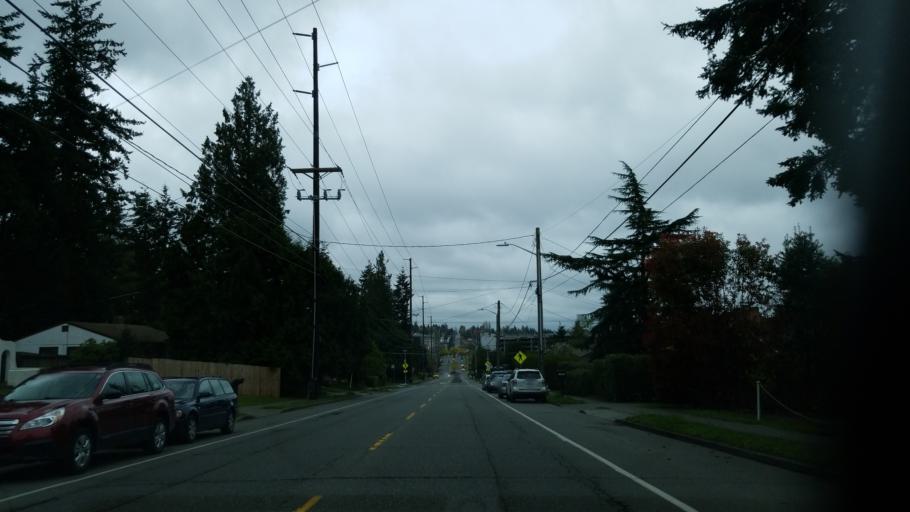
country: US
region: Washington
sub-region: King County
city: Shoreline
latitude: 47.7134
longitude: -122.3234
